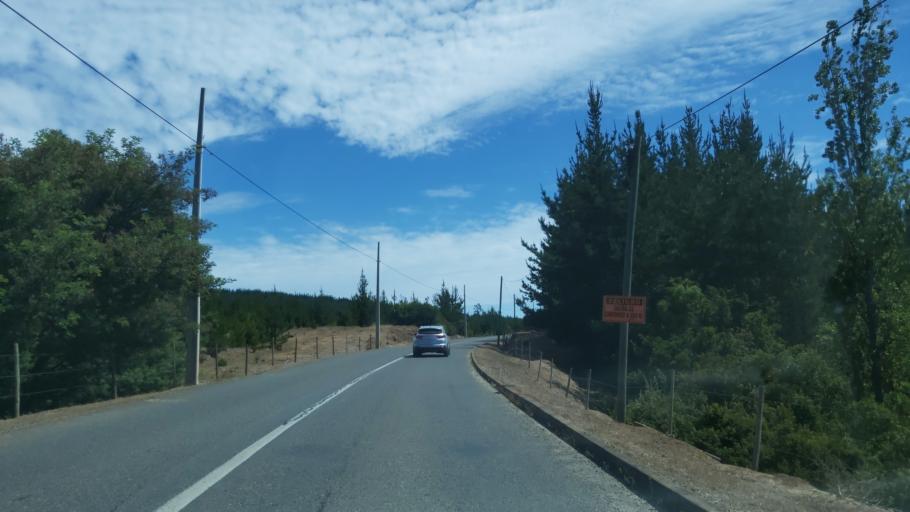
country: CL
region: Maule
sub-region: Provincia de Talca
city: Constitucion
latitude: -35.5175
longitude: -72.5306
